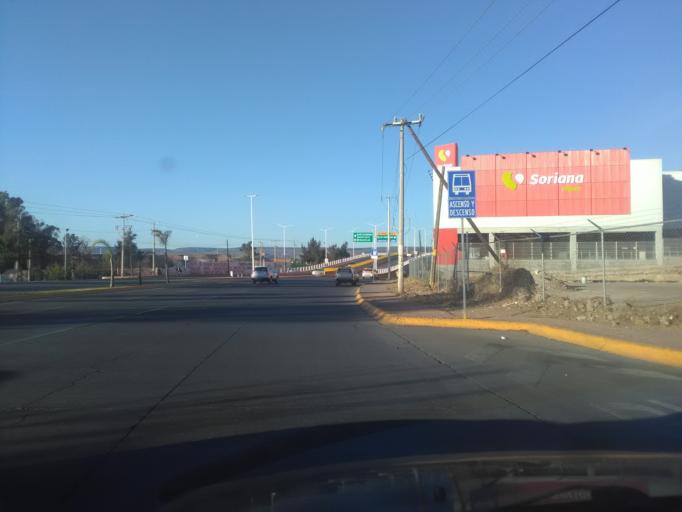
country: MX
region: Durango
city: Victoria de Durango
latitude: 24.0127
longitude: -104.6908
